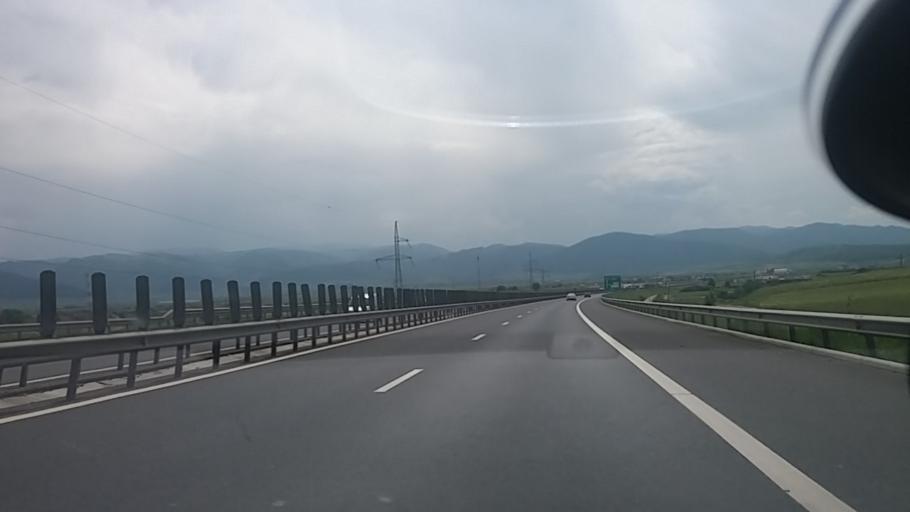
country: RO
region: Sibiu
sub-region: Comuna Cristian
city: Cristian
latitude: 45.7929
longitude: 24.0197
